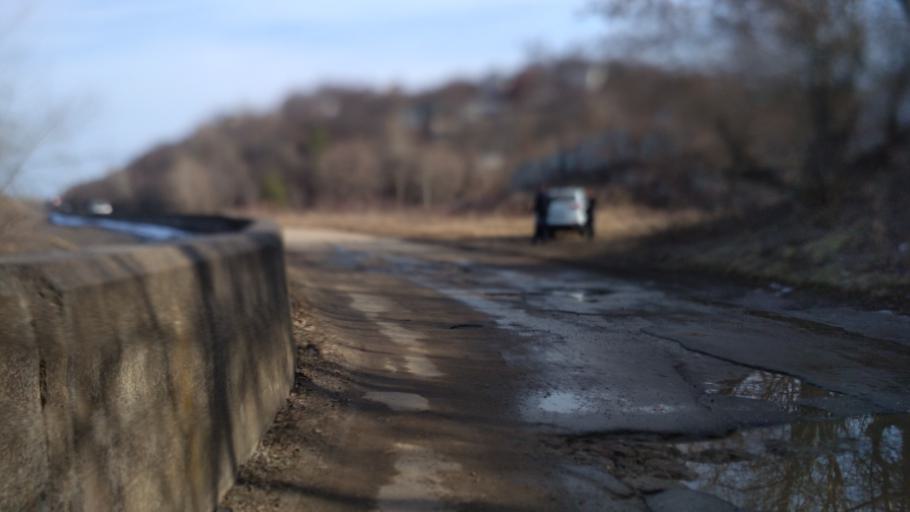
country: RU
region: Chuvashia
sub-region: Cheboksarskiy Rayon
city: Cheboksary
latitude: 56.1483
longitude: 47.2931
